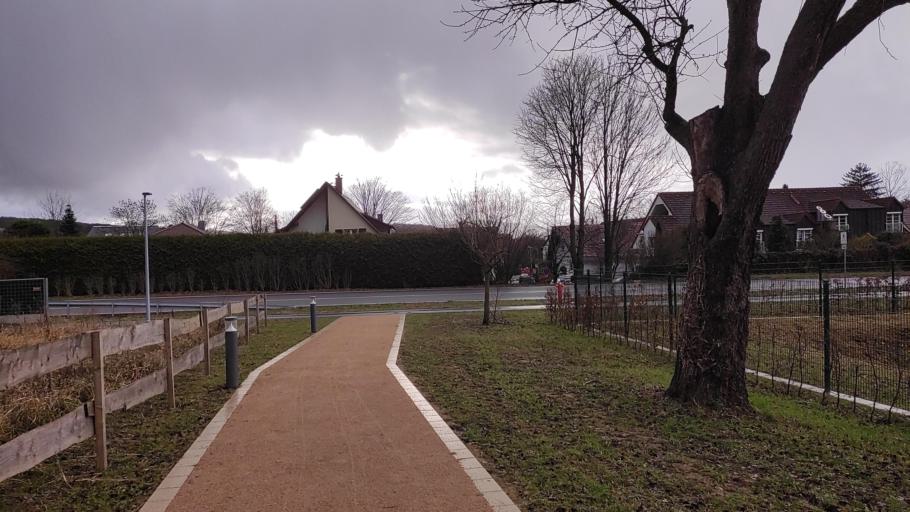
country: DE
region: Baden-Wuerttemberg
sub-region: Freiburg Region
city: Mullheim
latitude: 47.8098
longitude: 7.6383
